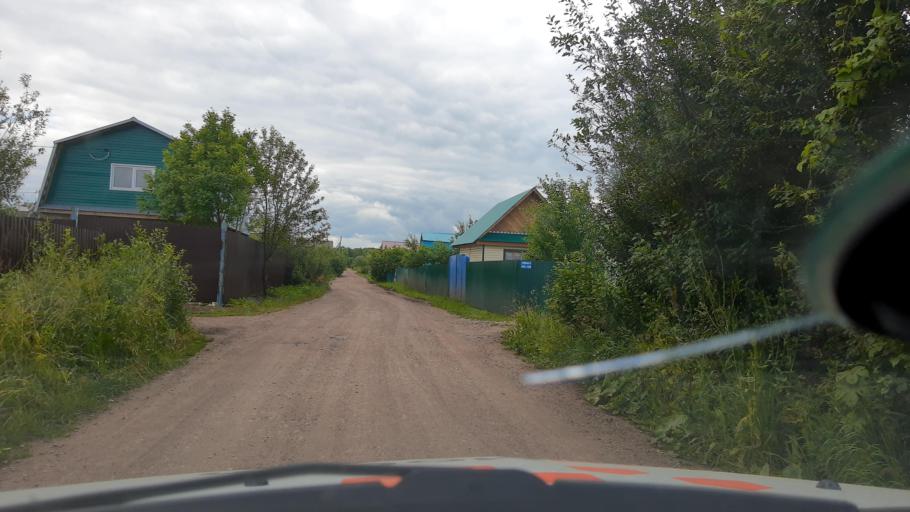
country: RU
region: Bashkortostan
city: Kabakovo
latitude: 54.7229
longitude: 56.2059
